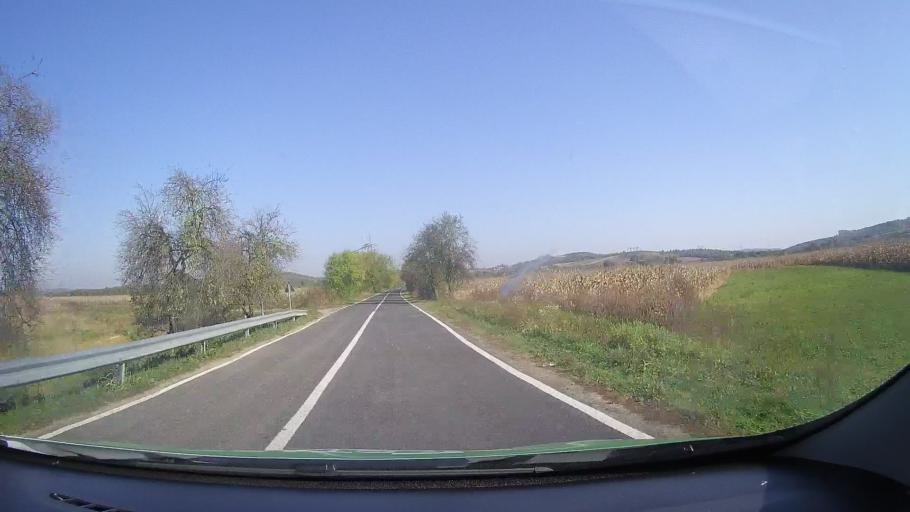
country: RO
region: Timis
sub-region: Comuna Curtea
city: Curtea
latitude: 45.8359
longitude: 22.3092
